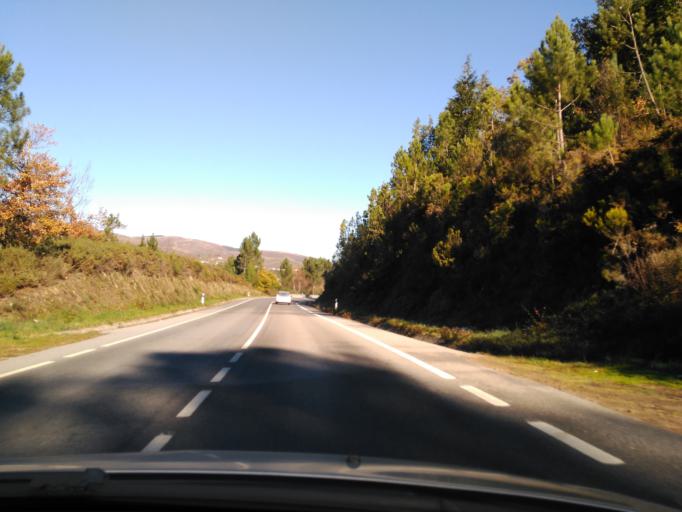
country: PT
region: Braga
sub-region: Cabeceiras de Basto
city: Cabeceiras de Basto
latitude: 41.6914
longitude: -7.9468
